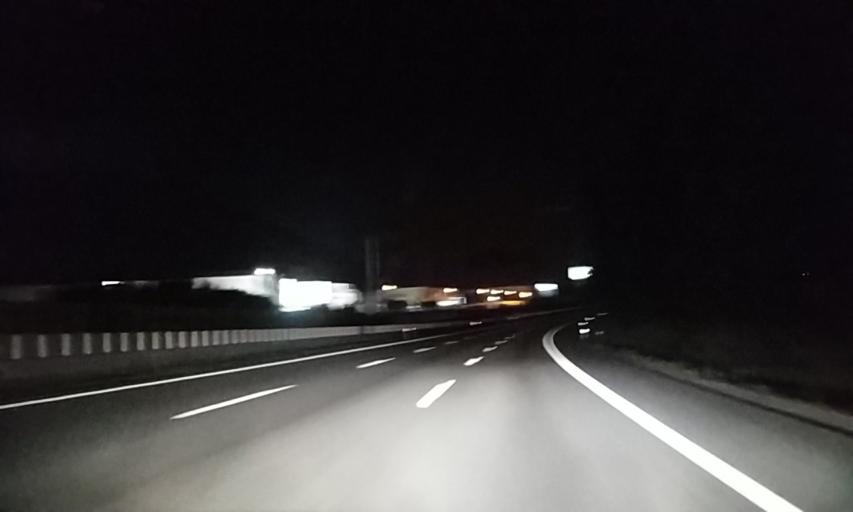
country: PT
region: Aveiro
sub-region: Santa Maria da Feira
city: Pacos de Brandao
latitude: 40.9905
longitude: -8.5855
